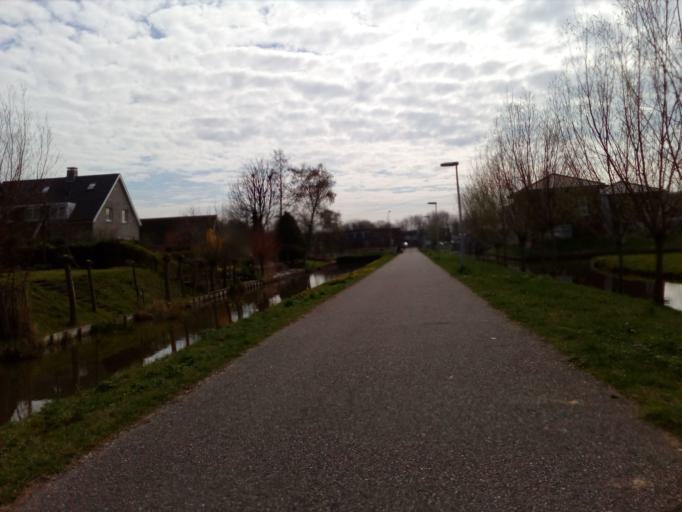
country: NL
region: South Holland
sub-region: Gemeente Den Haag
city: Ypenburg
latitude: 52.0403
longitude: 4.3797
